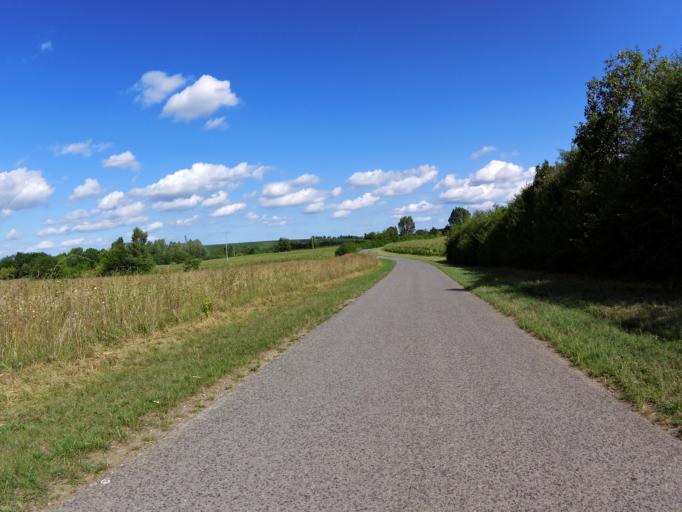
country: DE
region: Bavaria
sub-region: Regierungsbezirk Unterfranken
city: Sommerach
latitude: 49.8195
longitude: 10.2245
